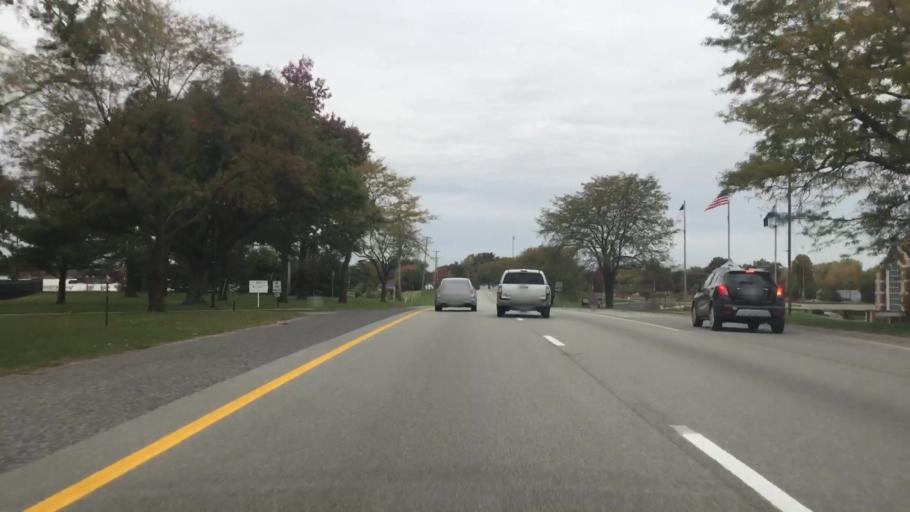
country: US
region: Missouri
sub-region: Jackson County
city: Raytown
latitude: 38.9830
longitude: -94.4566
